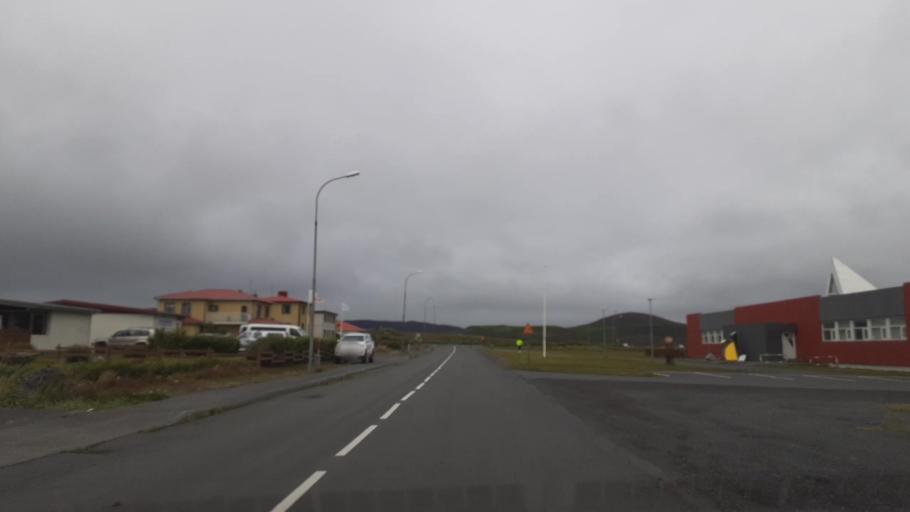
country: IS
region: Northeast
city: Husavik
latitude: 66.3014
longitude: -16.4481
